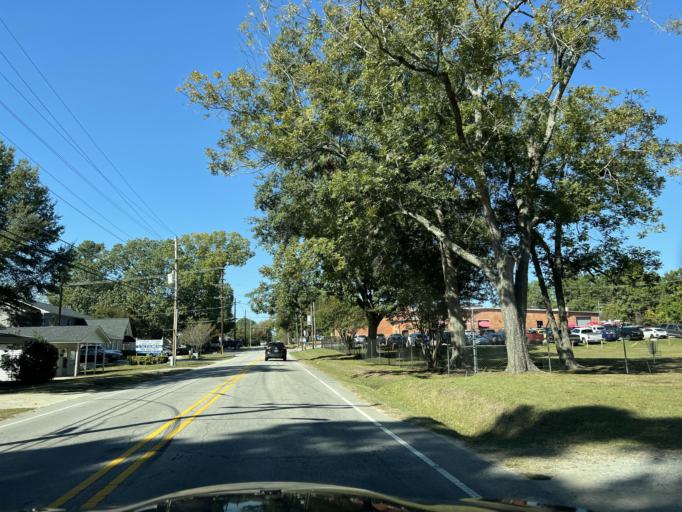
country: US
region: North Carolina
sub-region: Johnston County
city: Clayton
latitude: 35.6581
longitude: -78.4660
